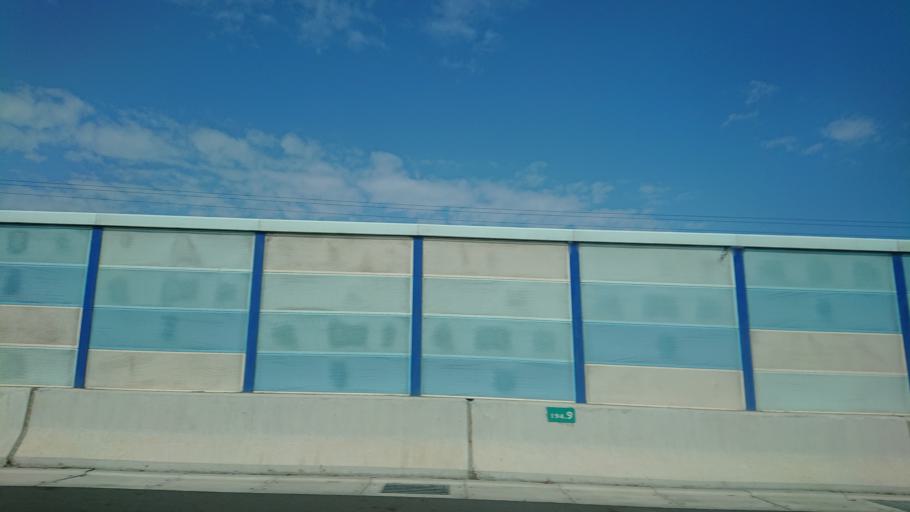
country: TW
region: Taiwan
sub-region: Changhua
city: Chang-hua
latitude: 23.9562
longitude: 120.3324
